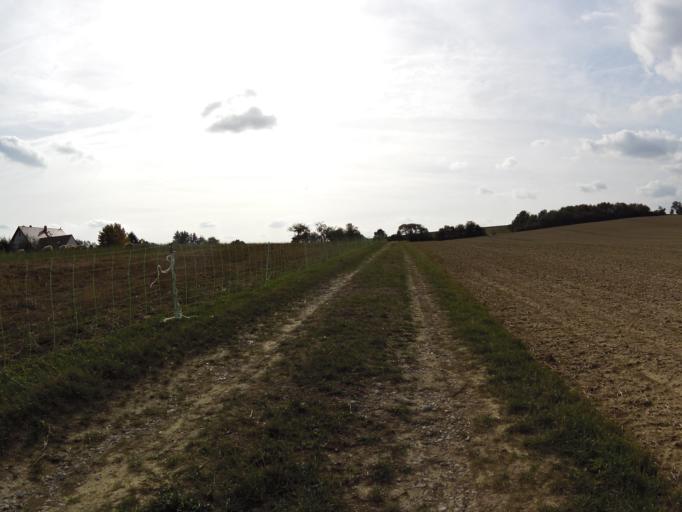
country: DE
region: Bavaria
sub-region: Regierungsbezirk Unterfranken
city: Eibelstadt
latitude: 49.7018
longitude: 9.9673
